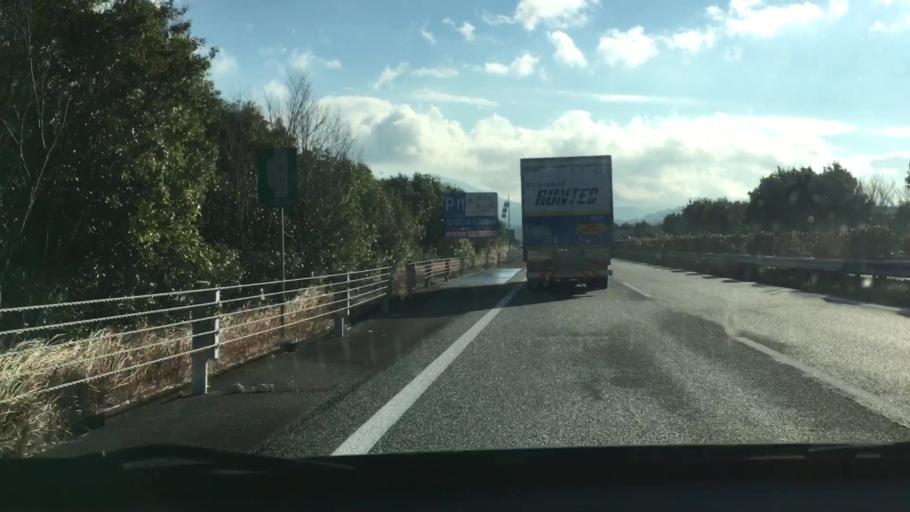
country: JP
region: Kumamoto
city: Hitoyoshi
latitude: 32.0593
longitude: 130.8033
